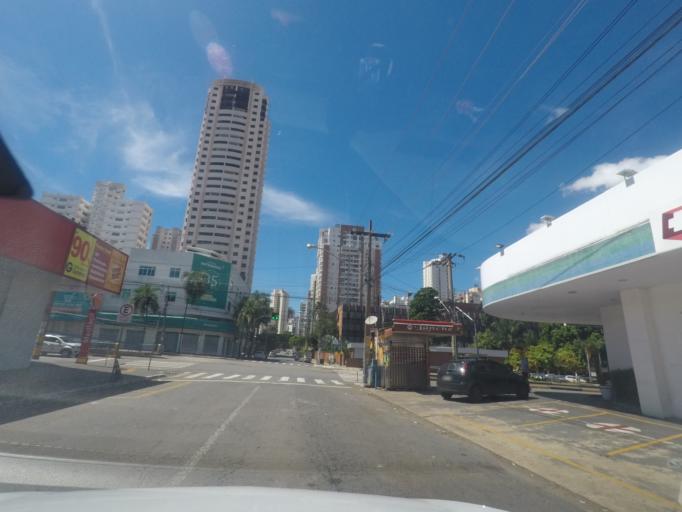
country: BR
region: Goias
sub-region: Goiania
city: Goiania
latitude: -16.6782
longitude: -49.2708
